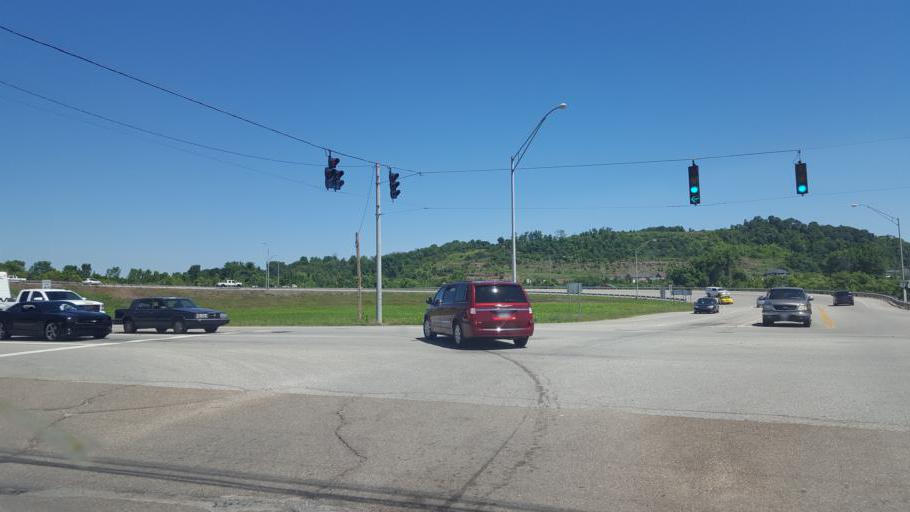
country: US
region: West Virginia
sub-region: Cabell County
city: Huntington
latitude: 38.4388
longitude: -82.3870
